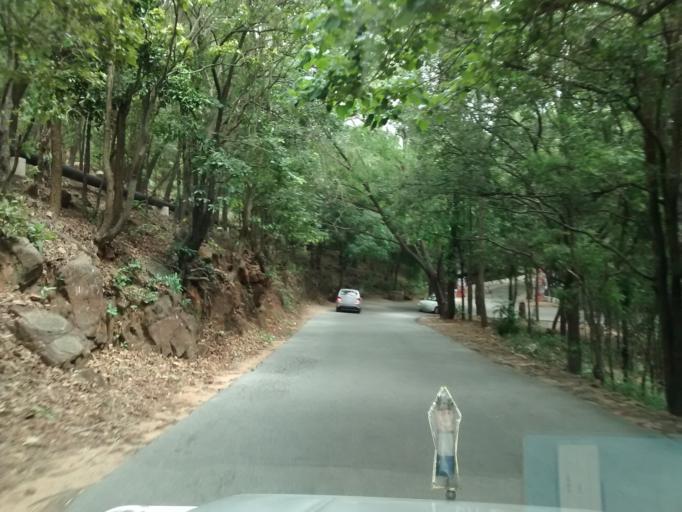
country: IN
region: Andhra Pradesh
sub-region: Chittoor
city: Tirumala
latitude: 13.7026
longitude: 79.3410
